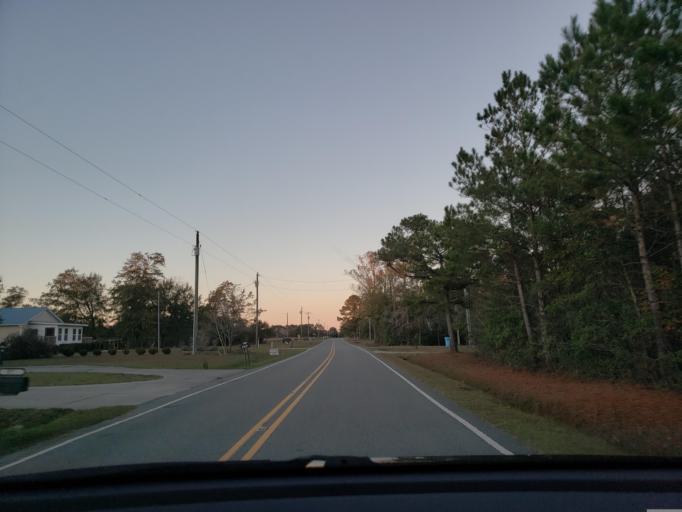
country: US
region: North Carolina
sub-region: Onslow County
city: Richlands
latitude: 34.7338
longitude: -77.6222
